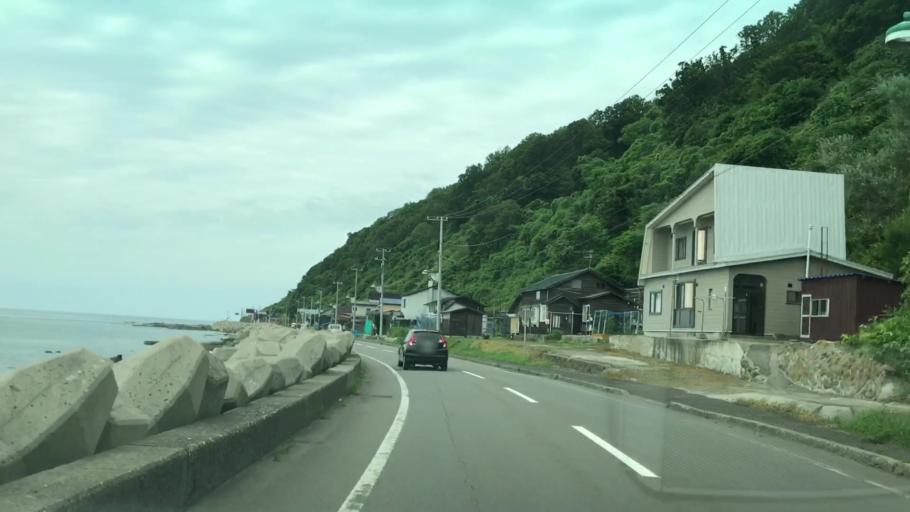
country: JP
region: Hokkaido
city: Iwanai
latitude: 43.1601
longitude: 140.3982
